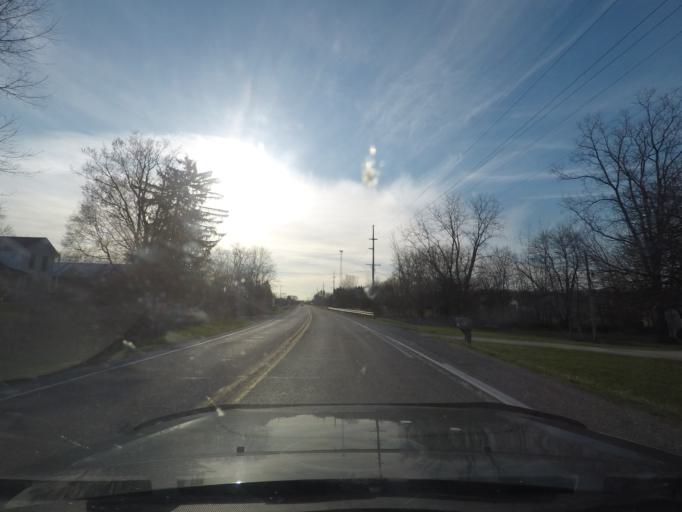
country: US
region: Indiana
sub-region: Saint Joseph County
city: Walkerton
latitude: 41.4513
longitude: -86.4459
